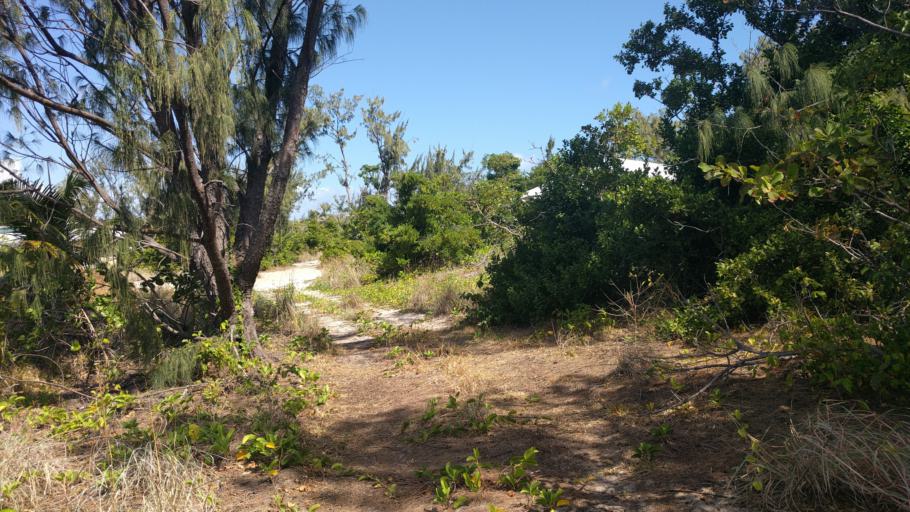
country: AU
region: Queensland
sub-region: Cook
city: Cooktown
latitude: -14.6782
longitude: 145.4476
